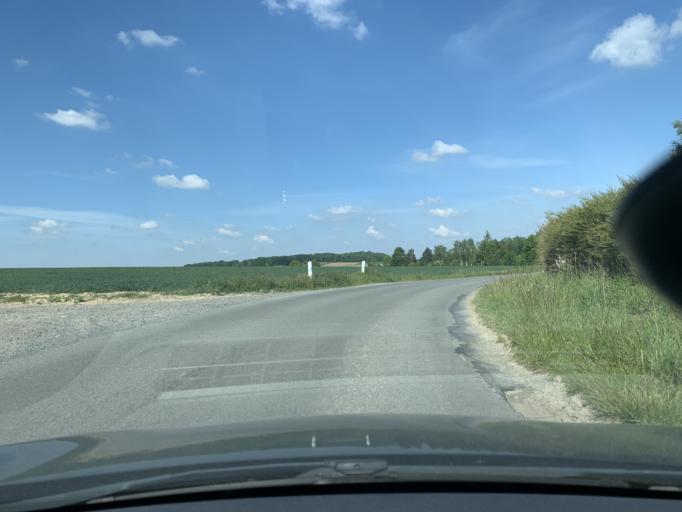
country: FR
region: Nord-Pas-de-Calais
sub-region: Departement du Nord
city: Aubigny-au-Bac
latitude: 50.2595
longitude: 3.1436
